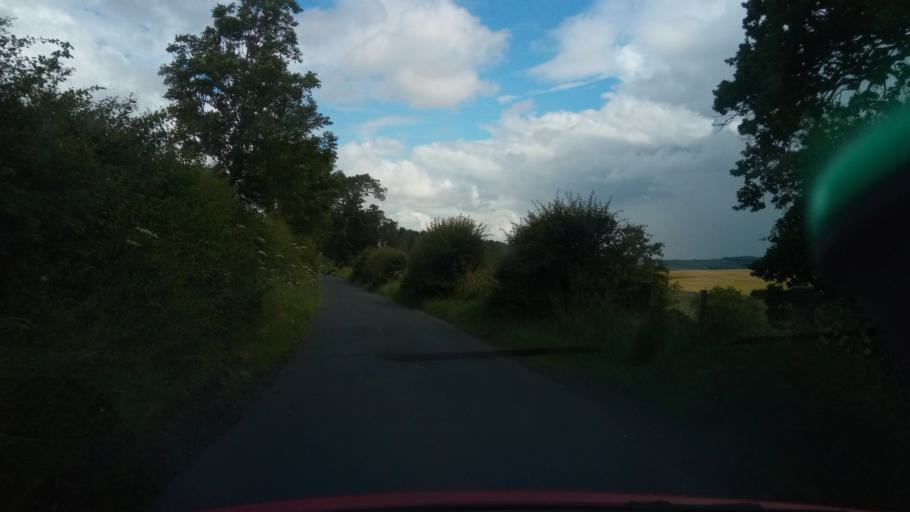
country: GB
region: Scotland
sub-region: The Scottish Borders
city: Kelso
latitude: 55.5084
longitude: -2.4209
